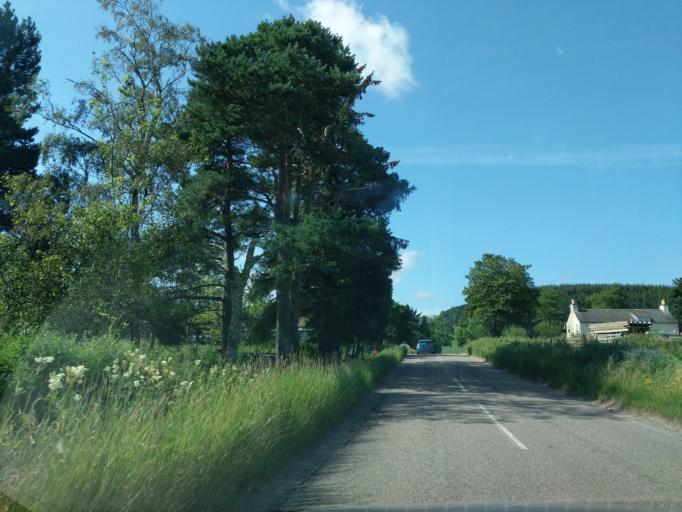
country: GB
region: Scotland
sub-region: Moray
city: Dufftown
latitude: 57.3503
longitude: -3.3046
